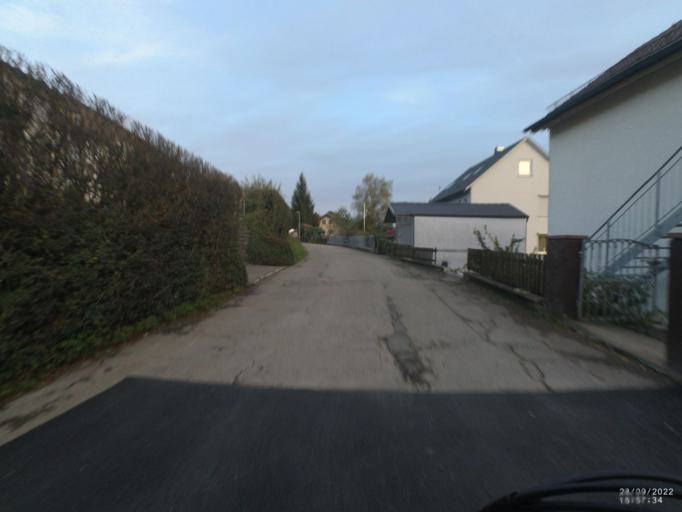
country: DE
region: Baden-Wuerttemberg
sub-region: Regierungsbezirk Stuttgart
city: Birenbach
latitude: 48.7492
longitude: 9.6483
